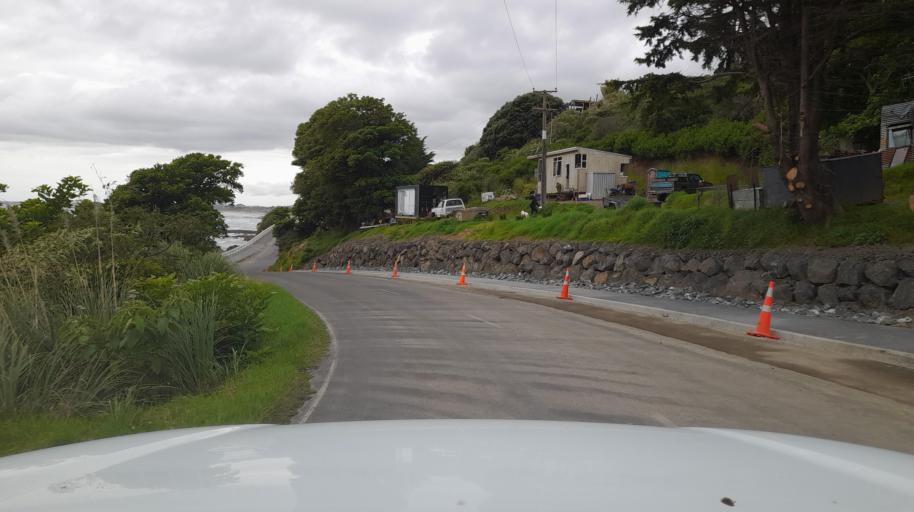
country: NZ
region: Northland
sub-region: Far North District
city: Ahipara
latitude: -35.1794
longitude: 173.1299
